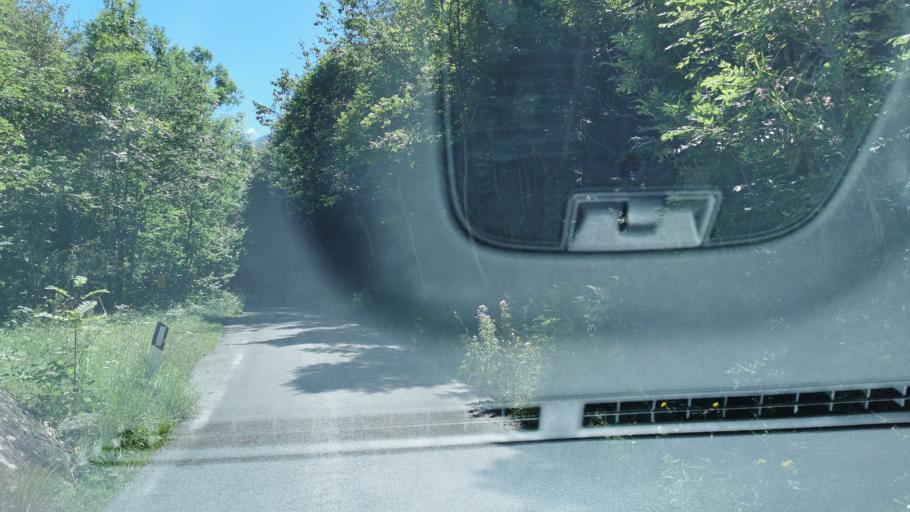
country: IT
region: Piedmont
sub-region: Provincia di Cuneo
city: Entracque
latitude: 44.1853
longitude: 7.3835
